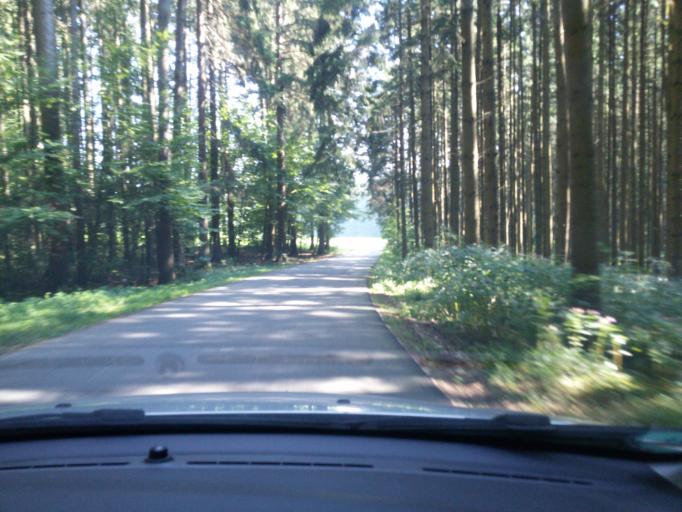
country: DE
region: Bavaria
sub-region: Swabia
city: Mittelneufnach
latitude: 48.2021
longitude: 10.6121
